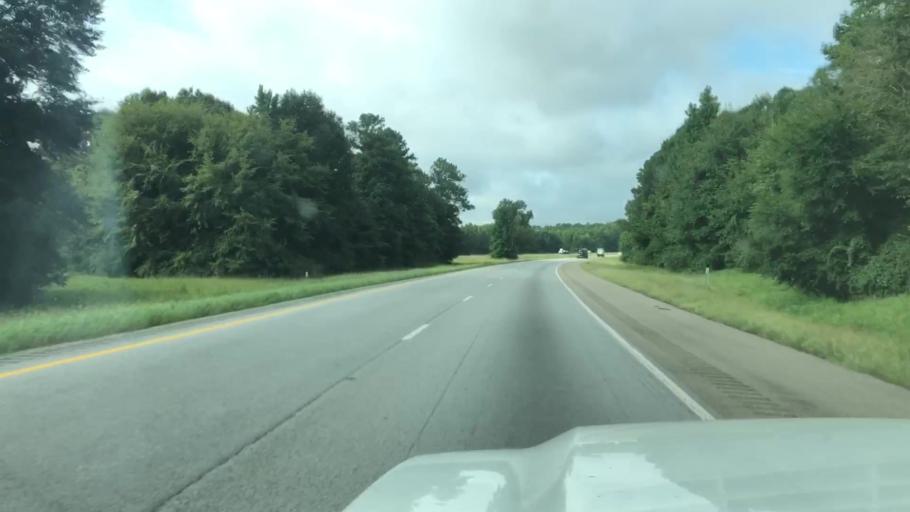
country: US
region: Alabama
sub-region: Lowndes County
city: Fort Deposit
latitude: 31.9675
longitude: -86.5371
